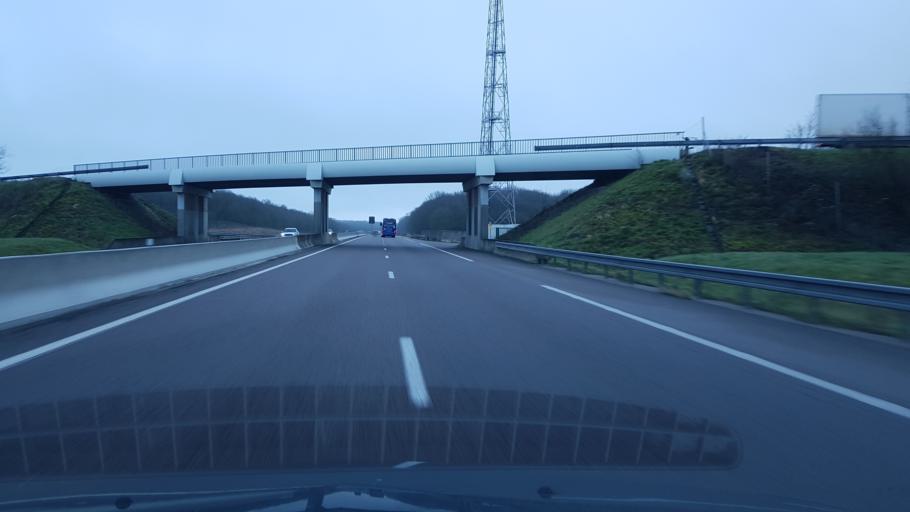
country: FR
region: Lorraine
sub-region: Departement de Meurthe-et-Moselle
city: Conflans-en-Jarnisy
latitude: 49.1808
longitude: 5.7885
